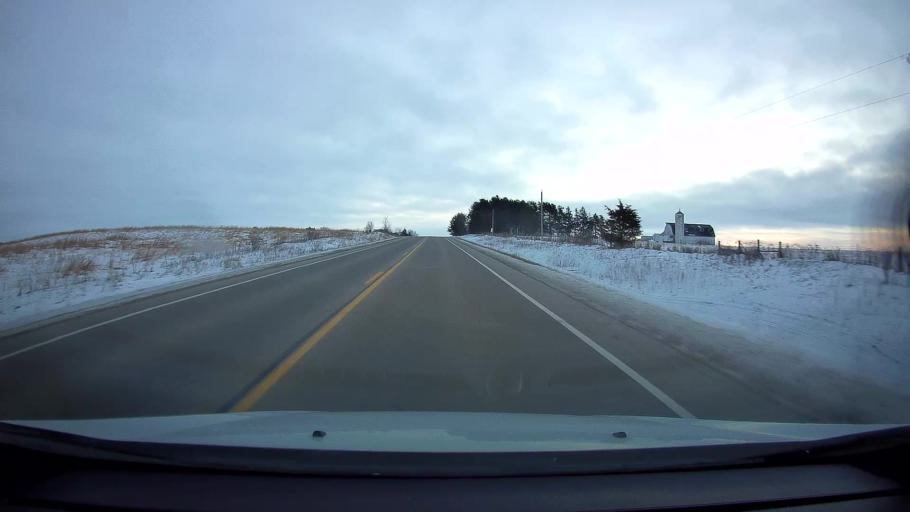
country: US
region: Wisconsin
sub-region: Saint Croix County
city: New Richmond
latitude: 45.1371
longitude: -92.5144
